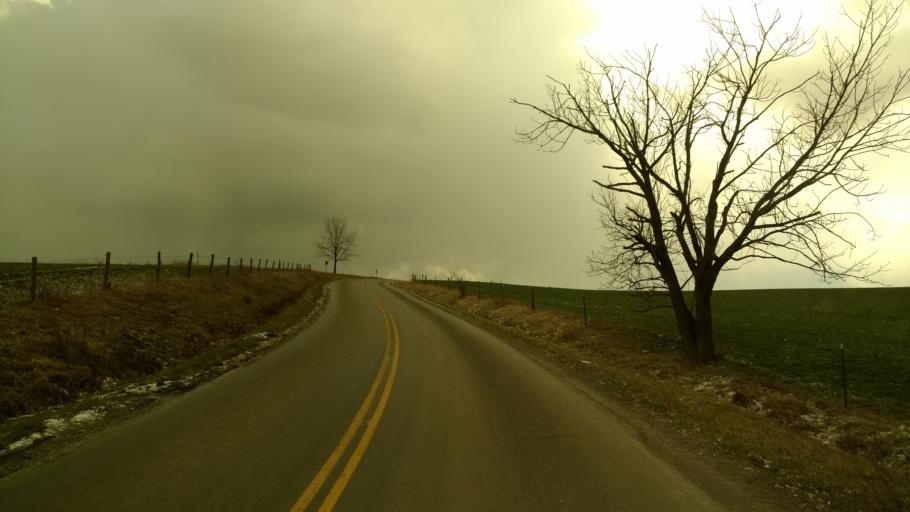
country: US
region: Ohio
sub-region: Tuscarawas County
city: Sugarcreek
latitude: 40.4649
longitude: -81.7771
